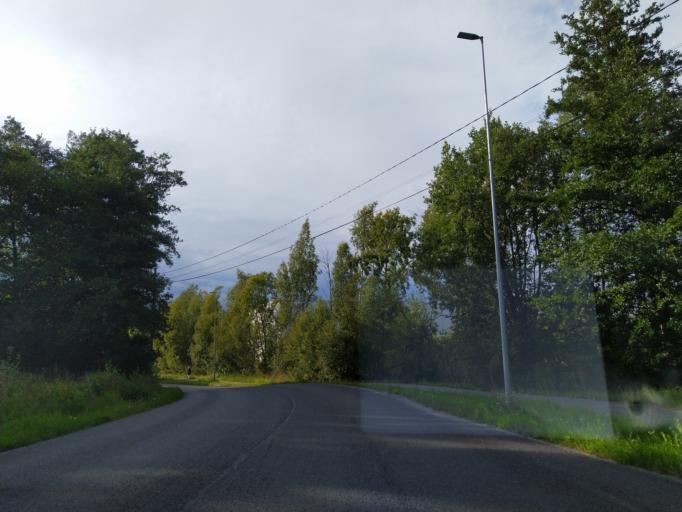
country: FI
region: Varsinais-Suomi
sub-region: Turku
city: Turku
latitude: 60.4290
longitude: 22.2238
